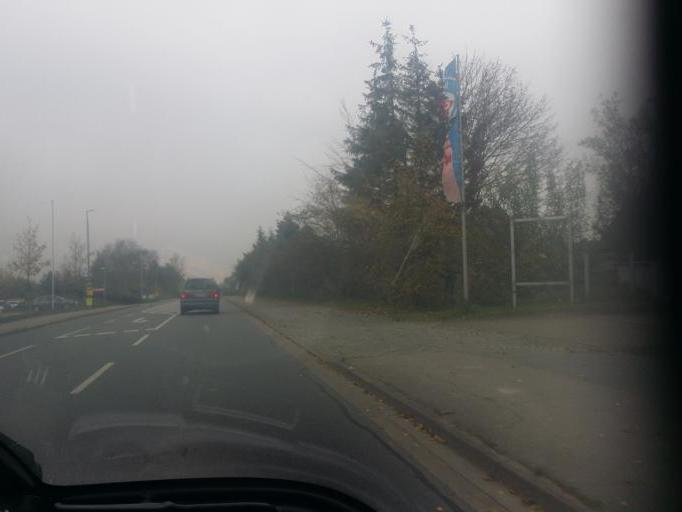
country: DE
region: Schleswig-Holstein
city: Husum
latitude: 54.4885
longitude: 9.0460
